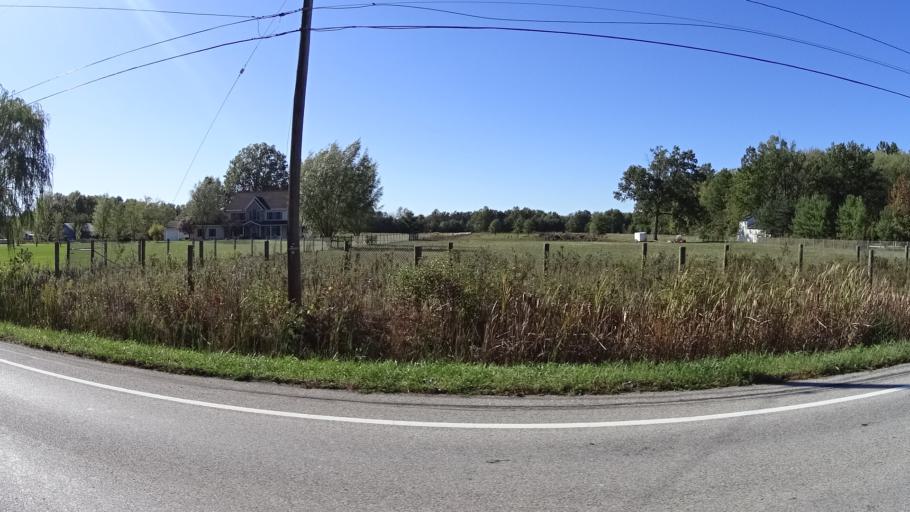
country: US
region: Ohio
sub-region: Lorain County
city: Amherst
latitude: 41.3944
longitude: -82.1647
